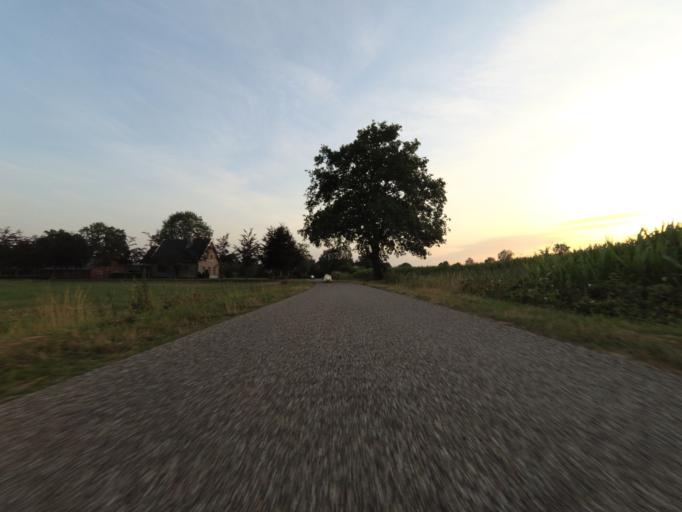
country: NL
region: Overijssel
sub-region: Gemeente Tubbergen
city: Tubbergen
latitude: 52.4130
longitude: 6.7630
